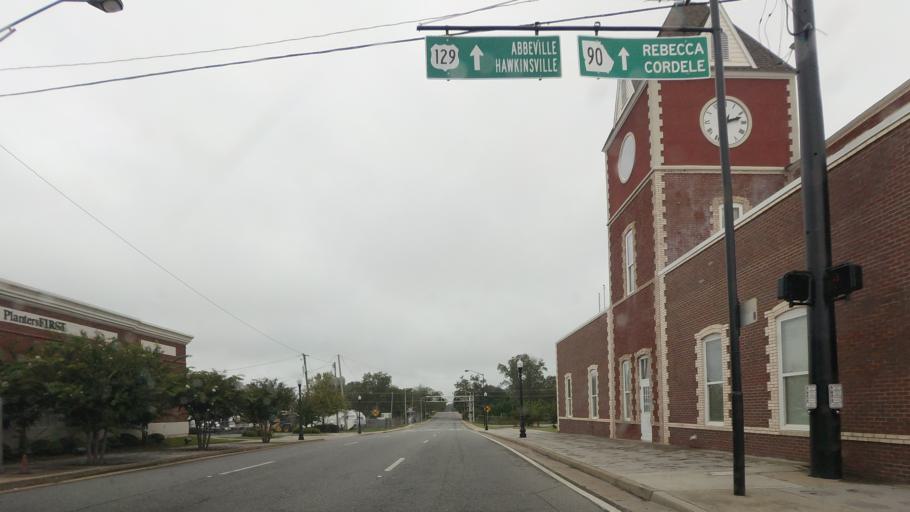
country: US
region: Georgia
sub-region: Ben Hill County
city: Fitzgerald
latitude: 31.7150
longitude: -83.2516
